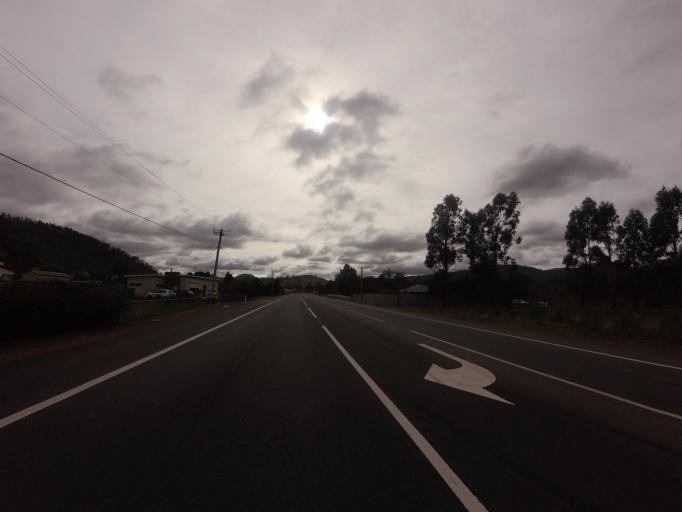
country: AU
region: Tasmania
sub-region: Brighton
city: Bridgewater
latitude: -42.6059
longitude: 147.2208
